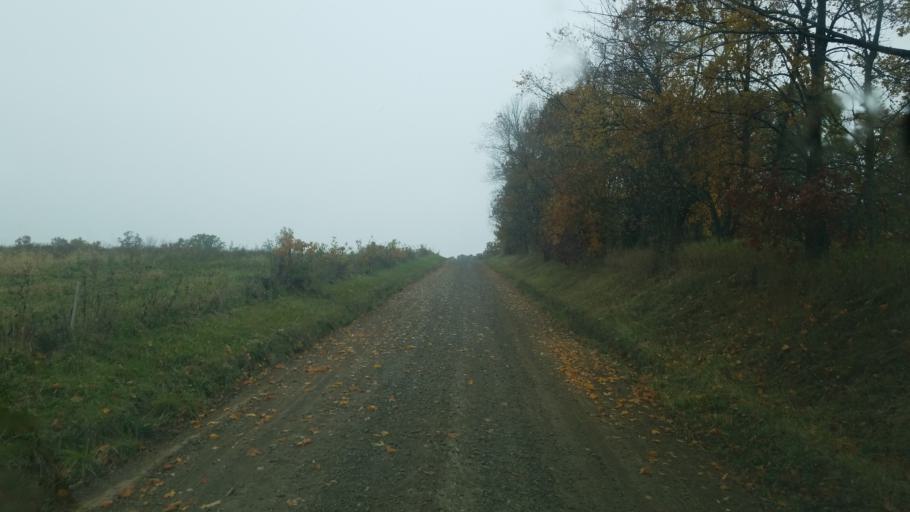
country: US
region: Ohio
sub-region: Holmes County
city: Millersburg
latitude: 40.4275
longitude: -81.8632
